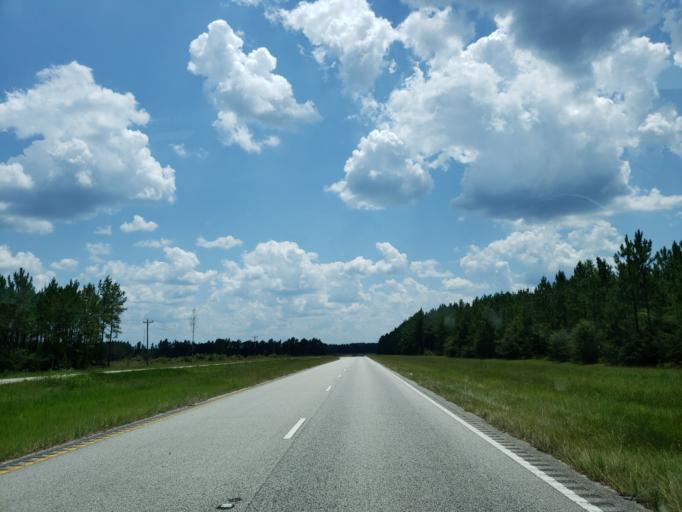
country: US
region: Mississippi
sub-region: Greene County
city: Leakesville
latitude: 31.2668
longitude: -88.5171
